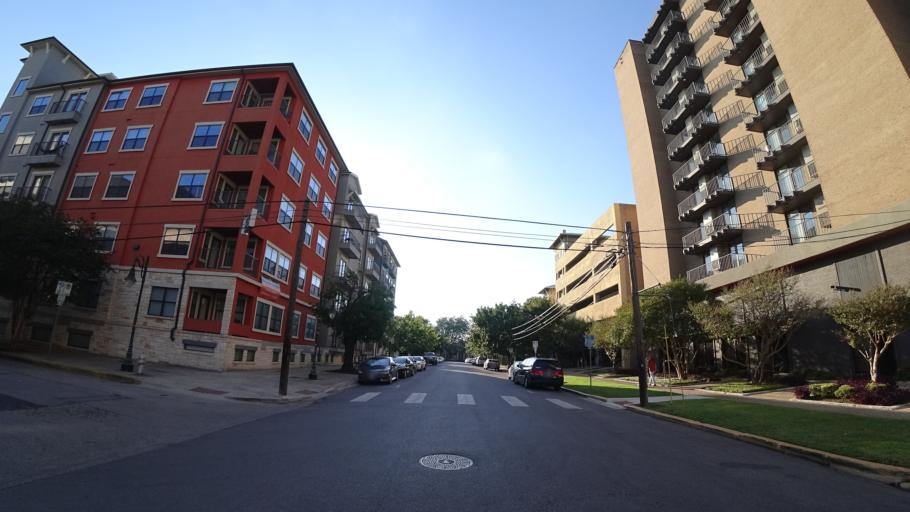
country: US
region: Texas
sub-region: Travis County
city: Austin
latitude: 30.2873
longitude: -97.7463
